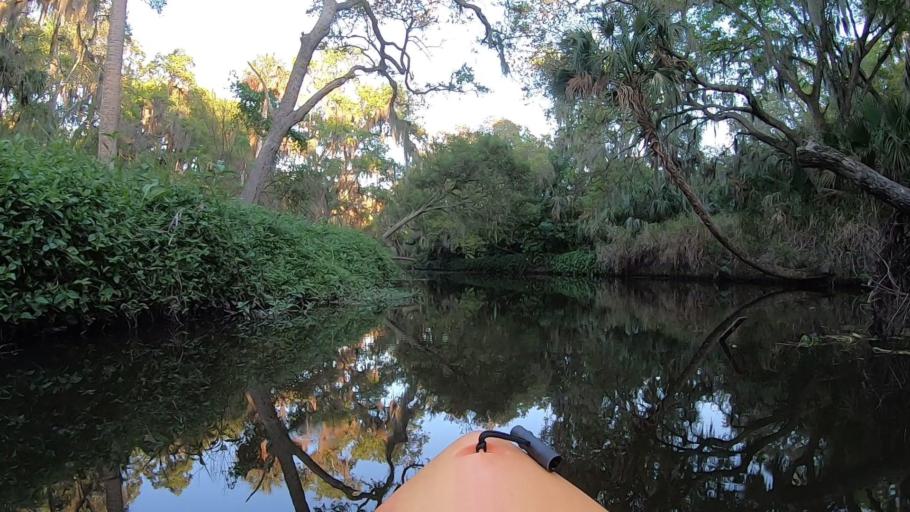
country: US
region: Florida
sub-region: Manatee County
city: Memphis
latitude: 27.5897
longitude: -82.5487
